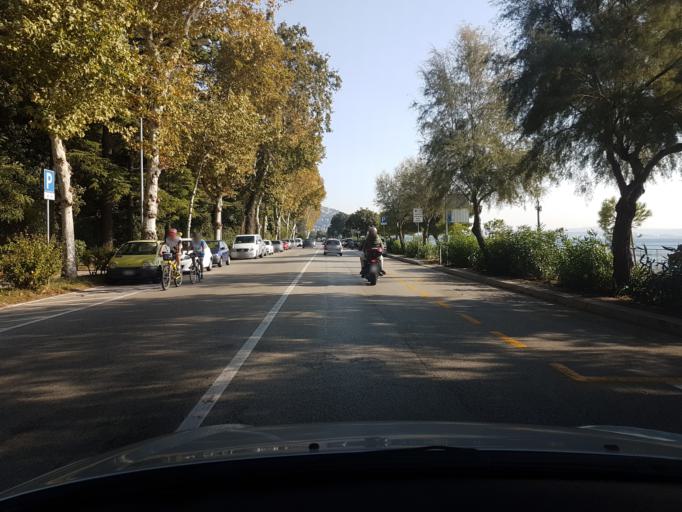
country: IT
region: Friuli Venezia Giulia
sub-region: Provincia di Trieste
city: Prosecco-Contovello
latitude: 45.6914
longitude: 13.7403
